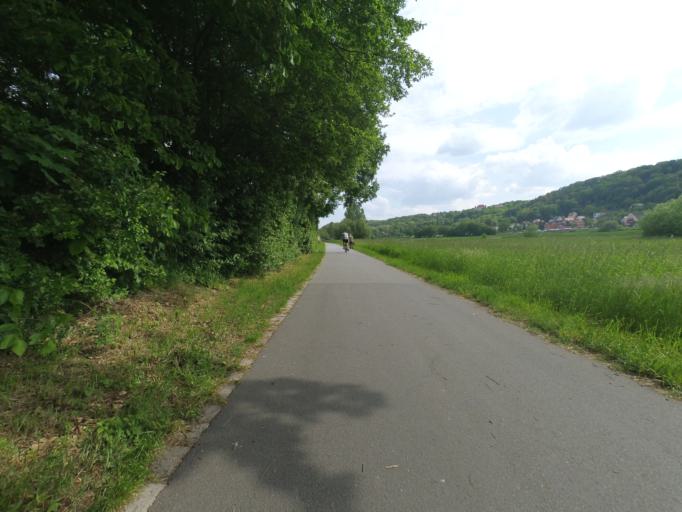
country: DE
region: Saxony
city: Meissen
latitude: 51.1569
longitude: 13.4823
